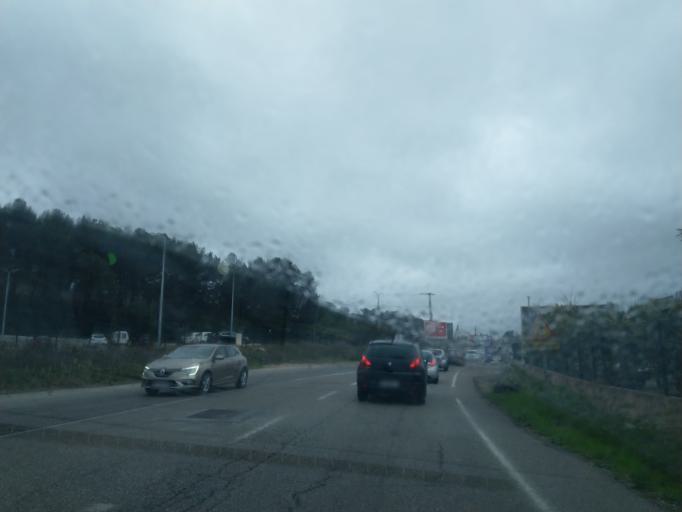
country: FR
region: Provence-Alpes-Cote d'Azur
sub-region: Departement des Bouches-du-Rhone
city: Septemes-les-Vallons
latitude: 43.4156
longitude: 5.3675
